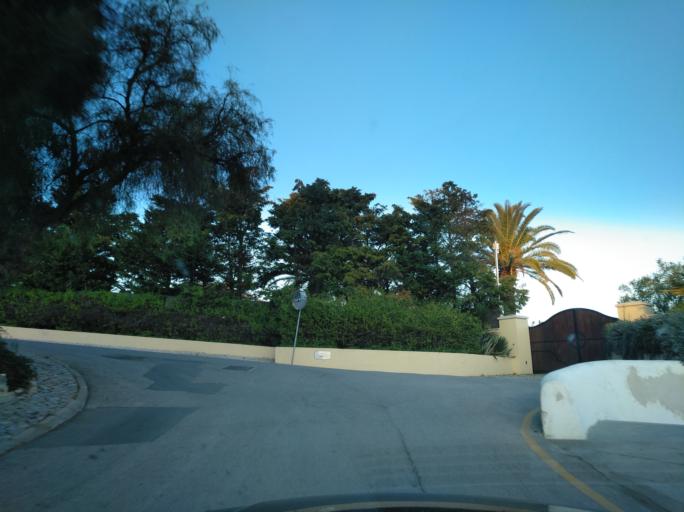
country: PT
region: Faro
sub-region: Tavira
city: Tavira
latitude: 37.1543
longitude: -7.5532
